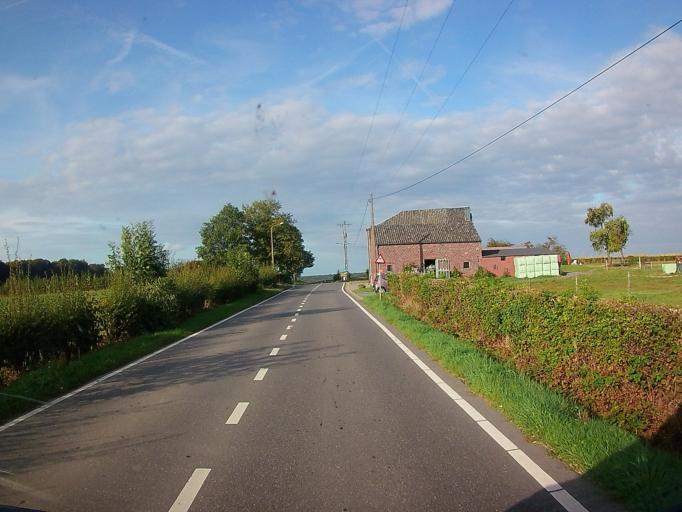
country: BE
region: Wallonia
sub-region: Province de Liege
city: Aubel
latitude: 50.7226
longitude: 5.8661
